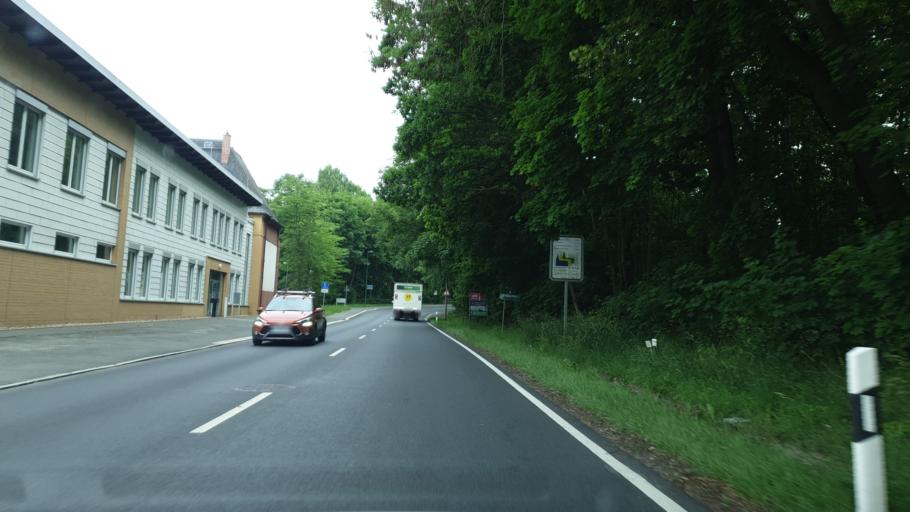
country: DE
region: Saxony
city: Auerbach
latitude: 50.5142
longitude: 12.4005
